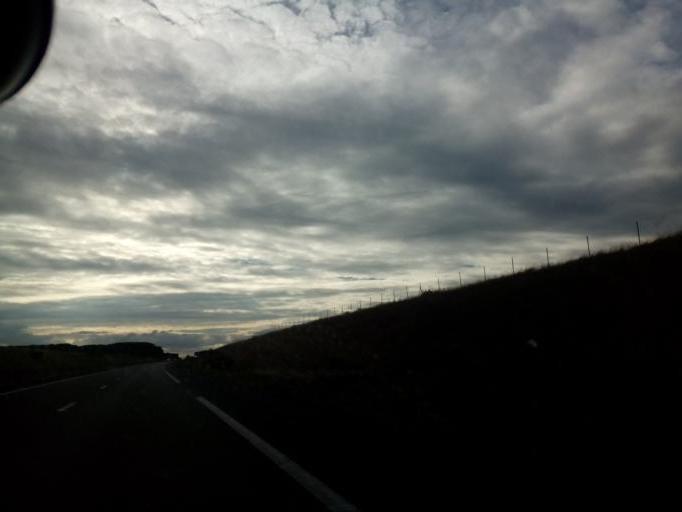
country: FR
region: Centre
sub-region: Departement d'Indre-et-Loire
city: Monts
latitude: 47.3065
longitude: 0.6374
